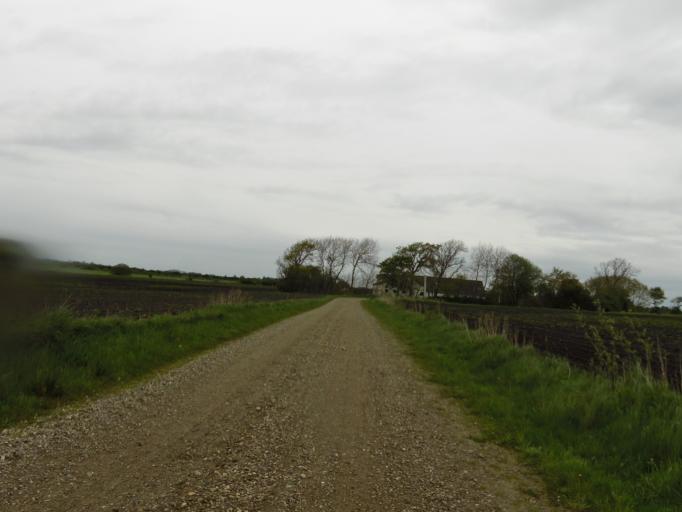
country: DK
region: South Denmark
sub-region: Haderslev Kommune
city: Gram
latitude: 55.2170
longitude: 8.9440
